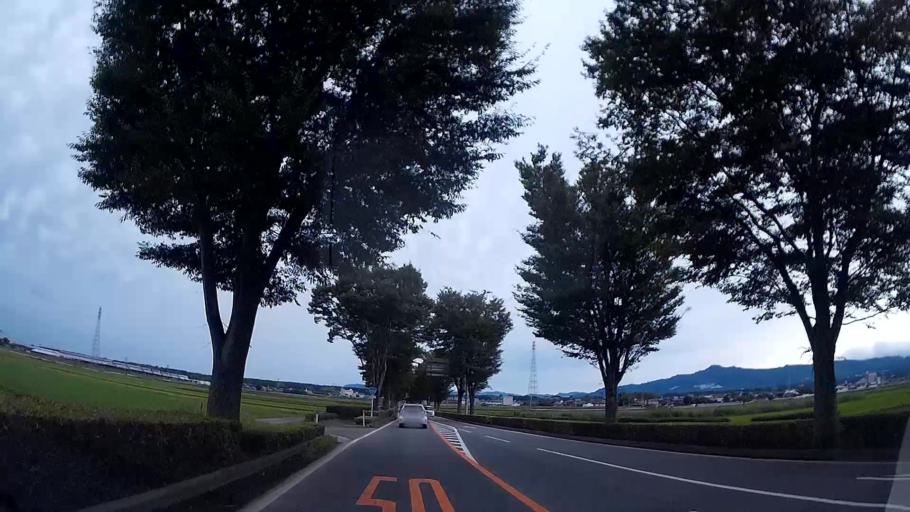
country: JP
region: Kumamoto
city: Ozu
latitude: 32.8581
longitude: 130.8552
